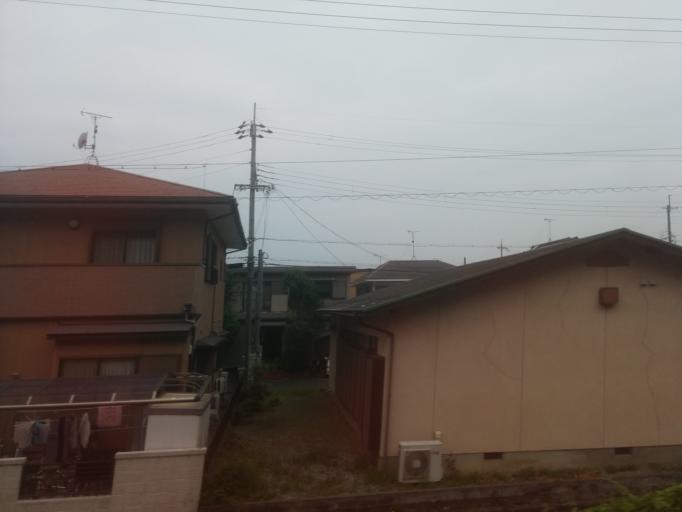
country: JP
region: Shiga Prefecture
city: Youkaichi
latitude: 35.1736
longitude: 136.1595
